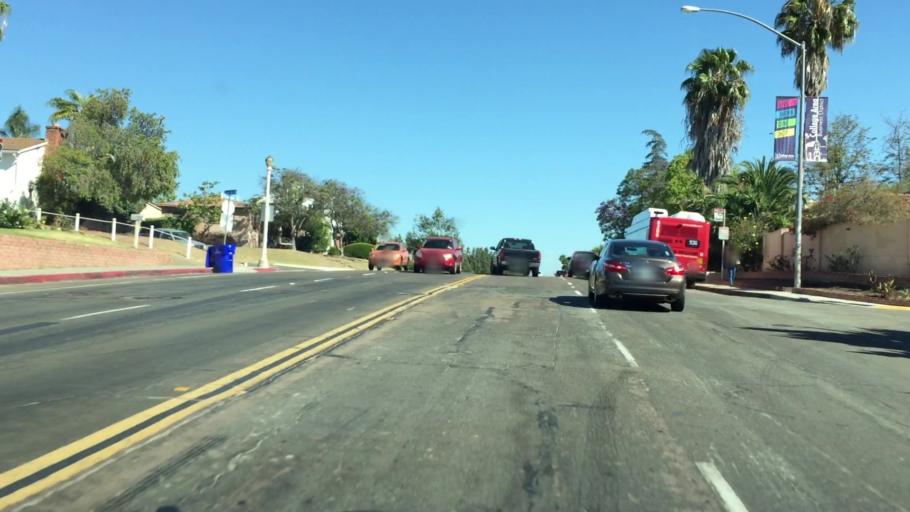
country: US
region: California
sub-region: San Diego County
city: Lemon Grove
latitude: 32.7688
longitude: -117.0688
